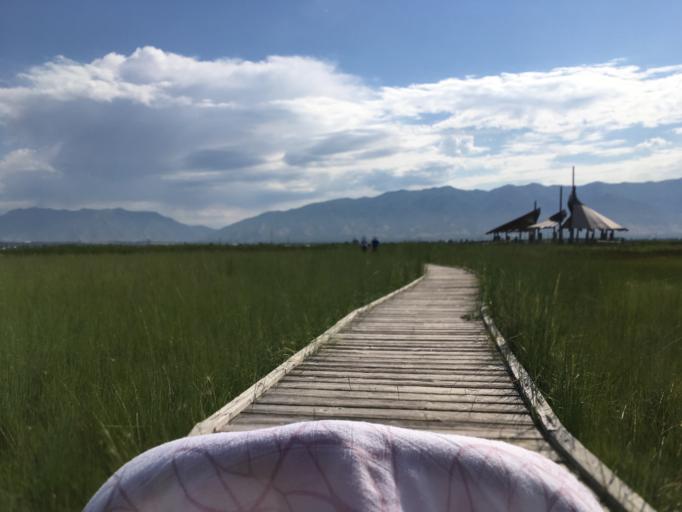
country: US
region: Utah
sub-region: Davis County
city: Layton
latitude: 41.0400
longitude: -112.0268
